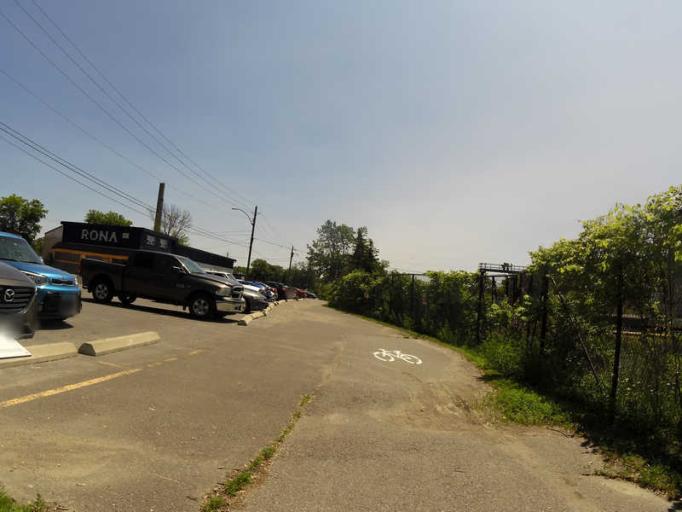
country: CA
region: Ontario
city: Peterborough
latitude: 44.4215
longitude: -78.2724
